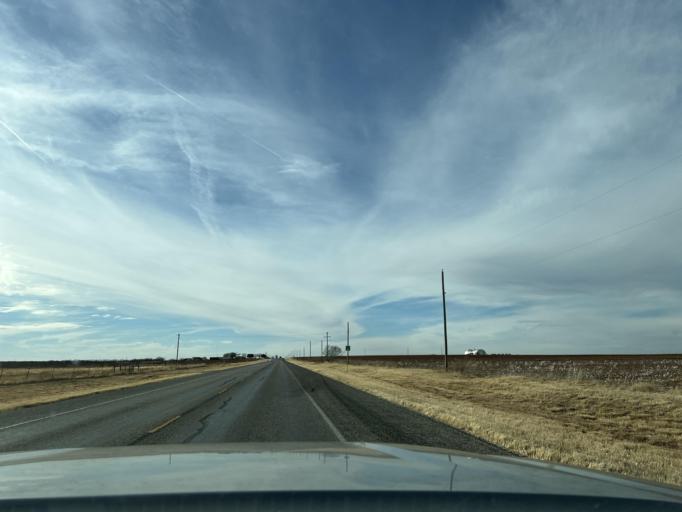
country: US
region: Texas
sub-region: Jones County
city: Anson
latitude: 32.7520
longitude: -99.9381
